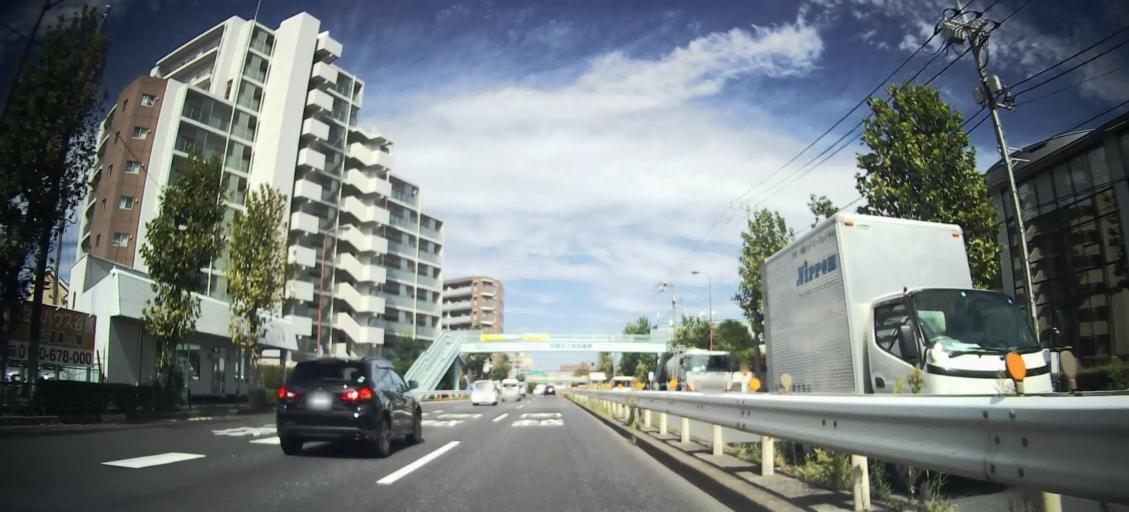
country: JP
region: Saitama
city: Wako
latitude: 35.7514
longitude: 139.6110
